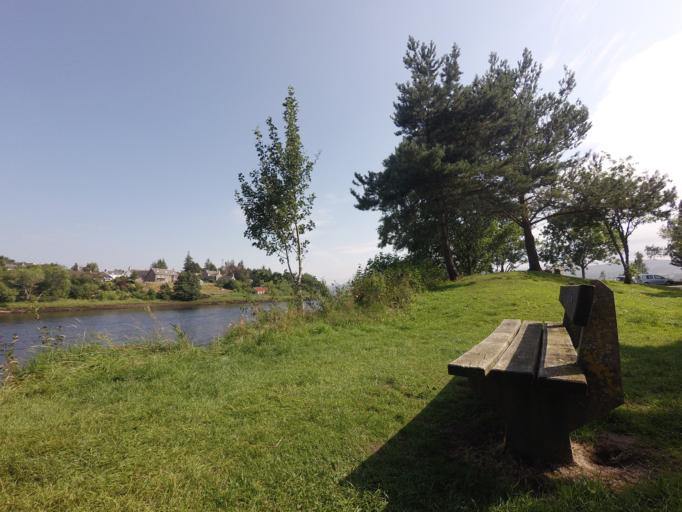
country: GB
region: Scotland
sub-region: Highland
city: Alness
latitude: 57.8904
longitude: -4.3482
